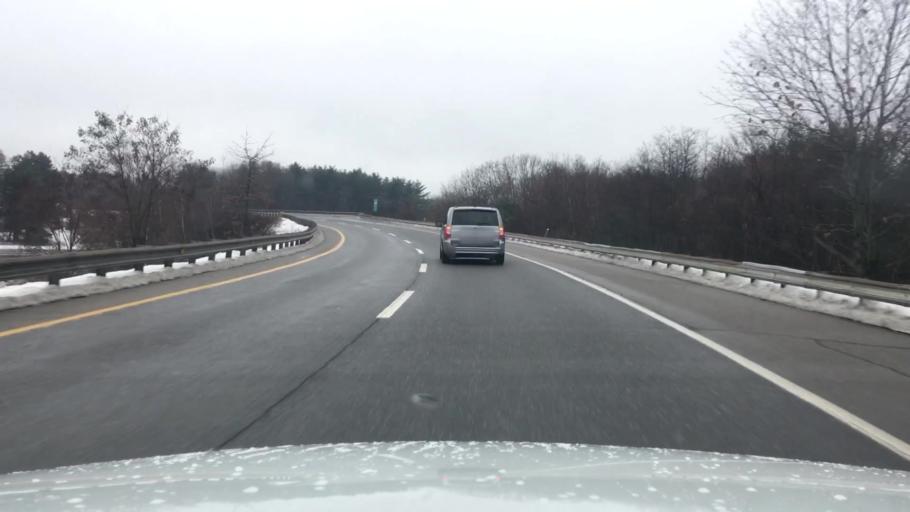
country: US
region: Maine
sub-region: Cumberland County
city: South Portland Gardens
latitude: 43.6300
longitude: -70.3173
